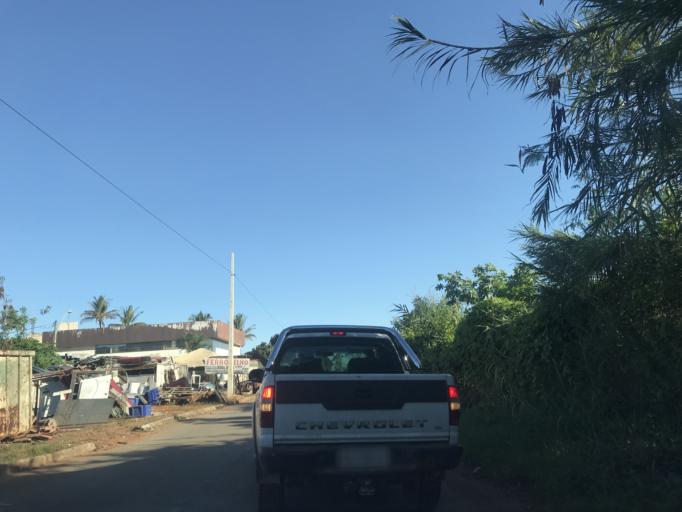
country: BR
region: Federal District
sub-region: Brasilia
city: Brasilia
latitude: -15.8189
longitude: -47.9576
